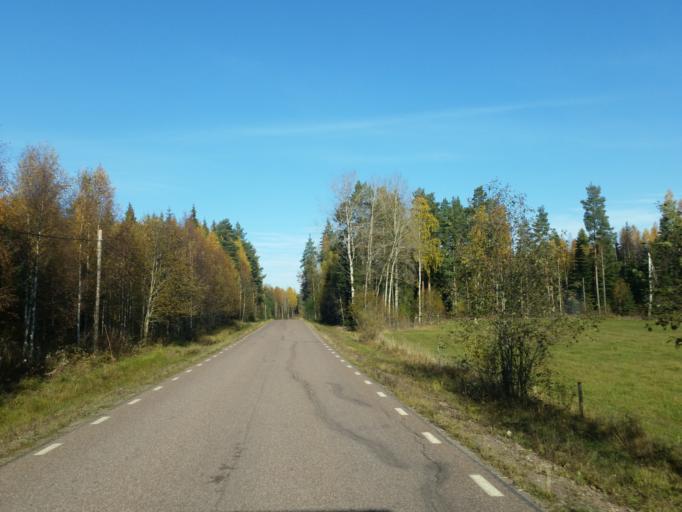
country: SE
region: Dalarna
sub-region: Borlange Kommun
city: Ornas
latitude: 60.4584
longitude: 15.6163
